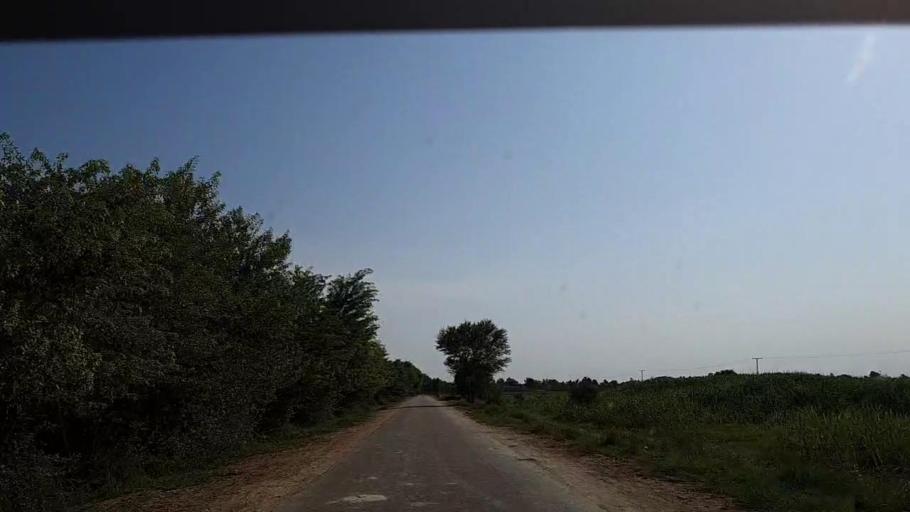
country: PK
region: Sindh
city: Adilpur
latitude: 27.9268
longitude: 69.2511
